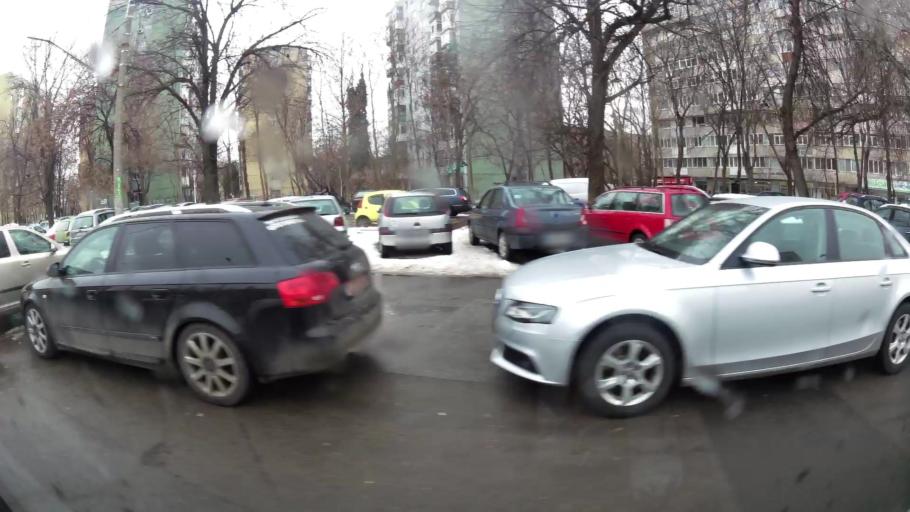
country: RO
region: Ilfov
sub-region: Comuna Chiajna
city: Rosu
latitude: 44.4166
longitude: 26.0219
